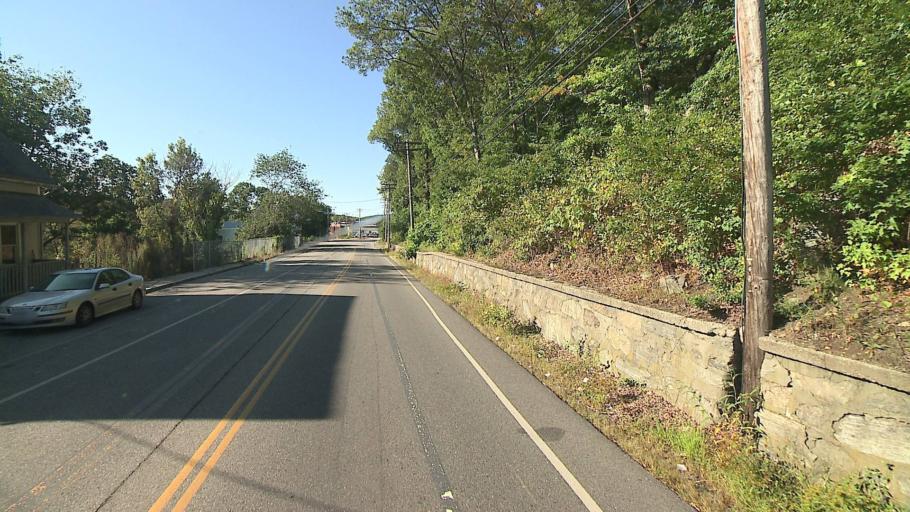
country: US
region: Connecticut
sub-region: New London County
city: Norwich
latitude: 41.5414
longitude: -72.0524
